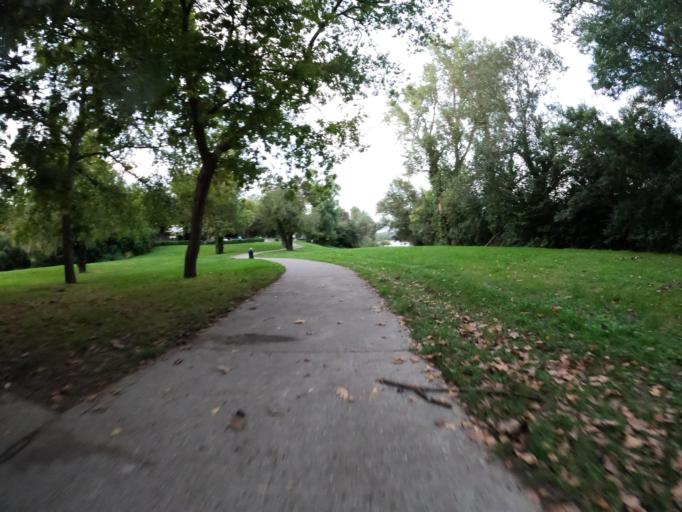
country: FR
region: Midi-Pyrenees
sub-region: Departement de la Haute-Garonne
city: Portet-sur-Garonne
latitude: 43.5221
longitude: 1.4114
